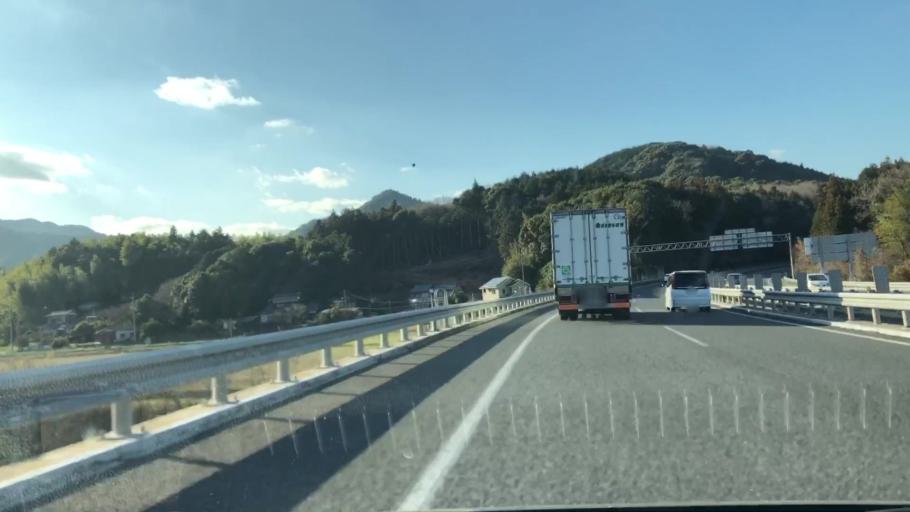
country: JP
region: Yamaguchi
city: Ogori-shimogo
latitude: 34.1728
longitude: 131.3136
